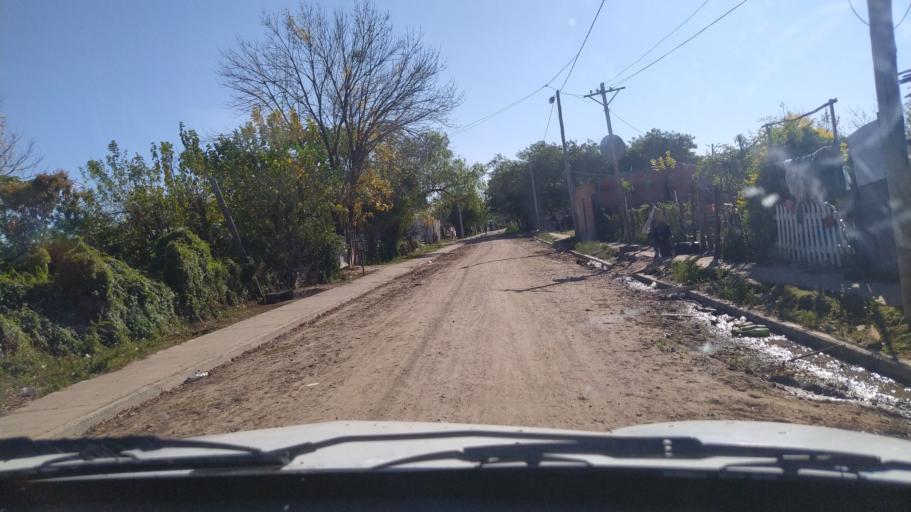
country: AR
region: Corrientes
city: Corrientes
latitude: -27.4979
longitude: -58.8046
